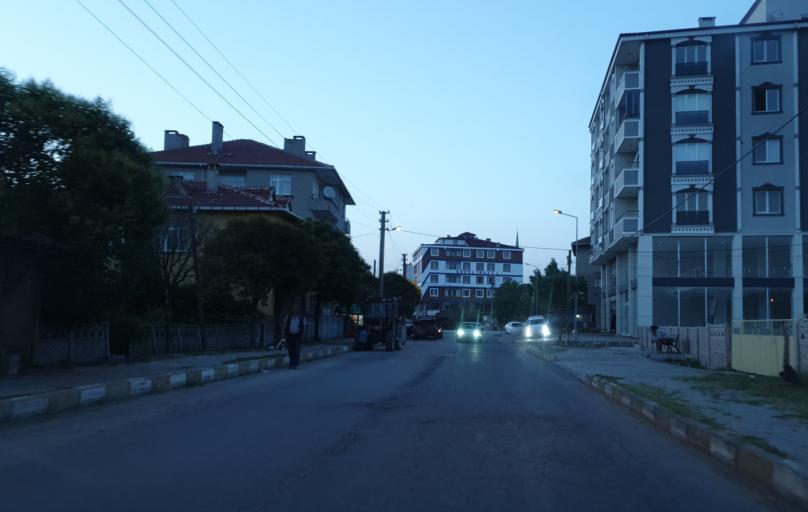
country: TR
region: Tekirdag
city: Saray
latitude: 41.3718
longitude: 27.9304
